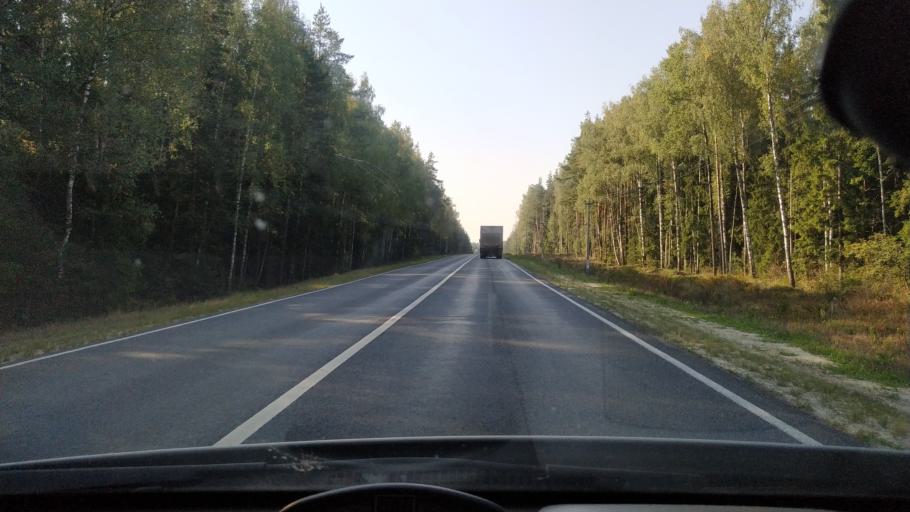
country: RU
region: Moskovskaya
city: Tugolesskiy Bor
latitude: 55.4970
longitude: 39.7141
